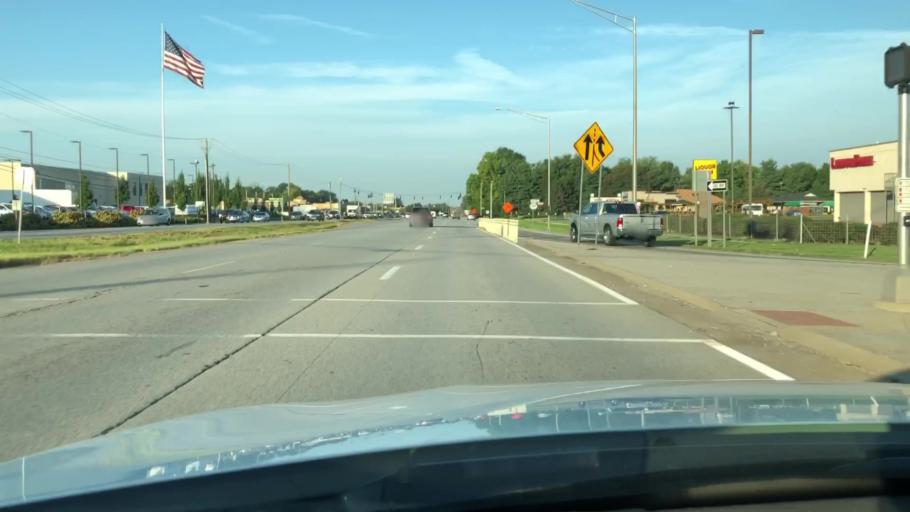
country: US
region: Kentucky
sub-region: Jefferson County
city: Hurstbourne Acres
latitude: 38.2203
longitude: -85.5817
